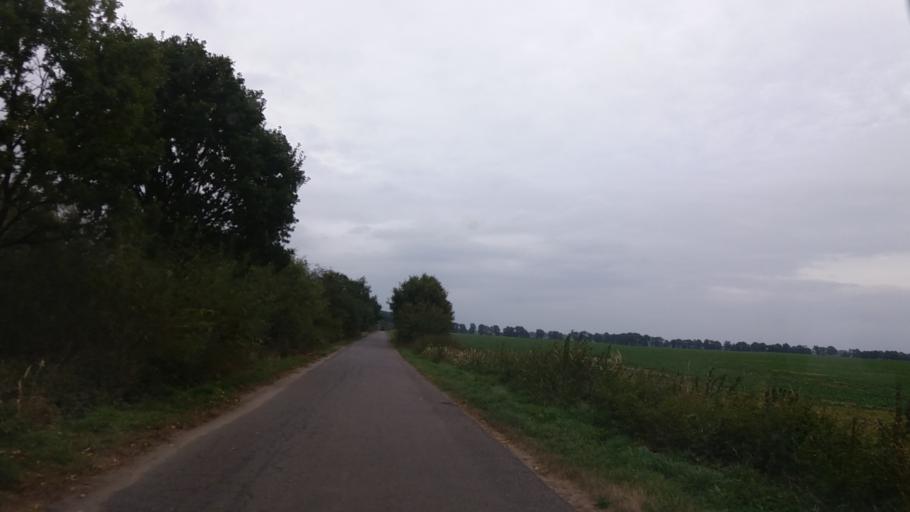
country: PL
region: West Pomeranian Voivodeship
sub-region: Powiat choszczenski
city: Krzecin
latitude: 52.9829
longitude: 15.5103
